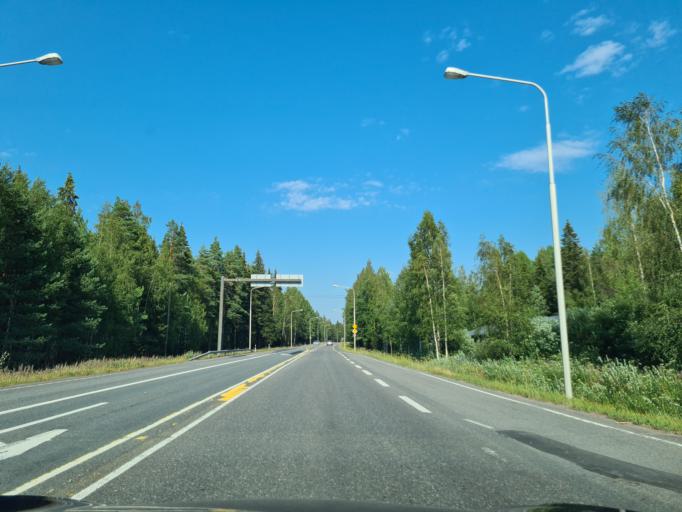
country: FI
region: Satakunta
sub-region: Pohjois-Satakunta
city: Kankaanpaeae
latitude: 61.8315
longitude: 22.4029
